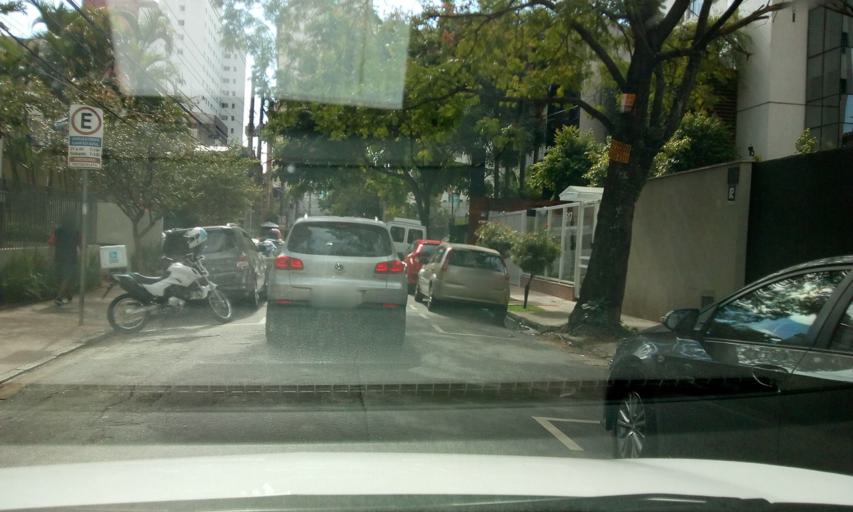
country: BR
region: Sao Paulo
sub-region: Sao Paulo
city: Sao Paulo
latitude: -23.5852
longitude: -46.6788
